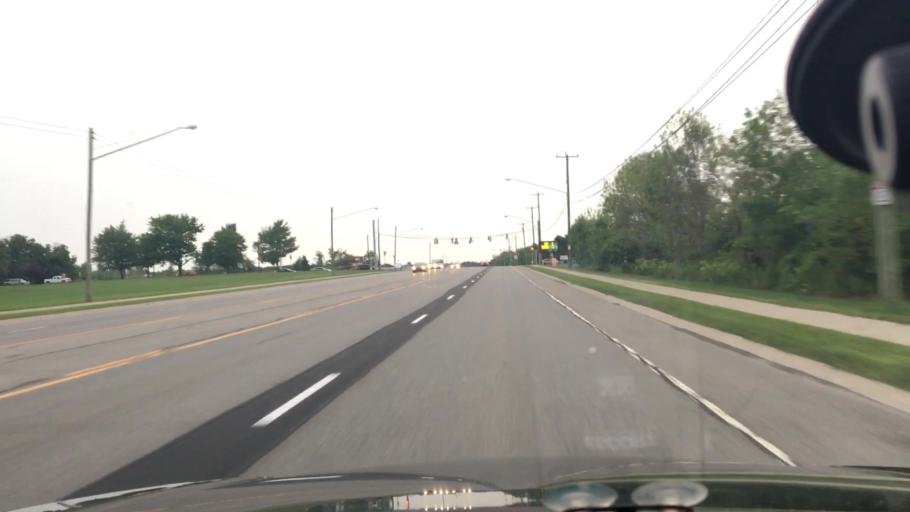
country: US
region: New York
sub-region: Erie County
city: Blasdell
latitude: 42.7749
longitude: -78.7986
